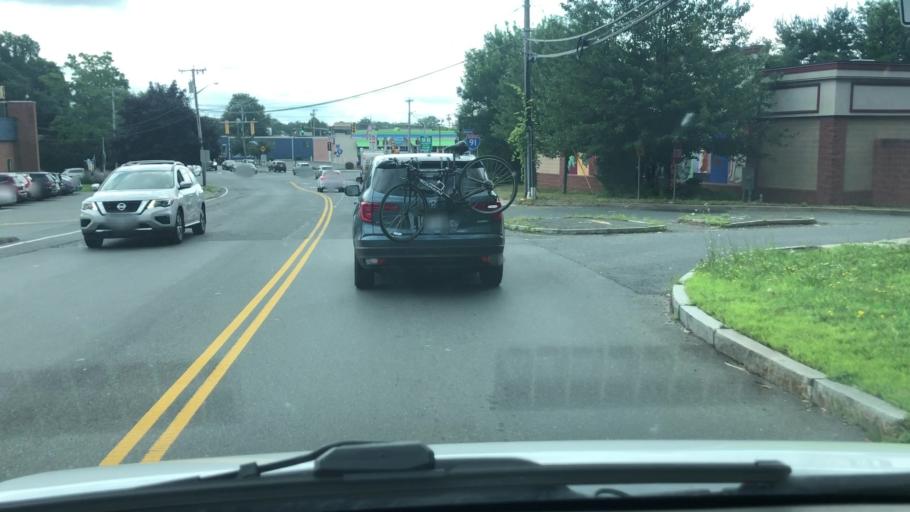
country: US
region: Massachusetts
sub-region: Hampshire County
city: Northampton
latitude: 42.3378
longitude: -72.6387
